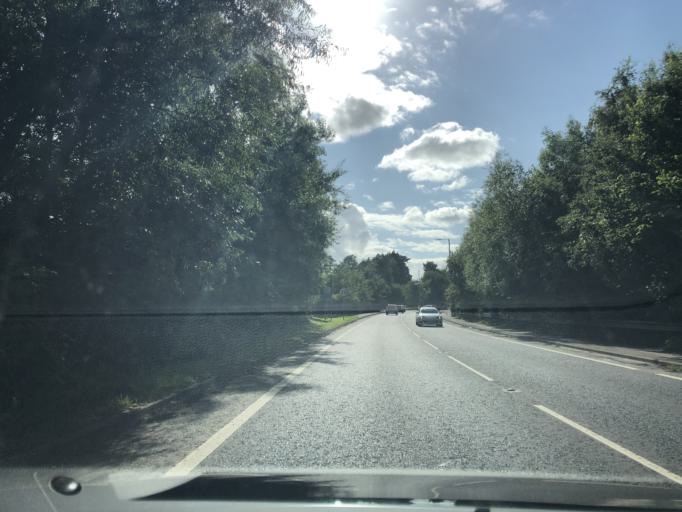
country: GB
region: Northern Ireland
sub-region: Ards District
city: Comber
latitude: 54.5473
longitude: -5.7402
